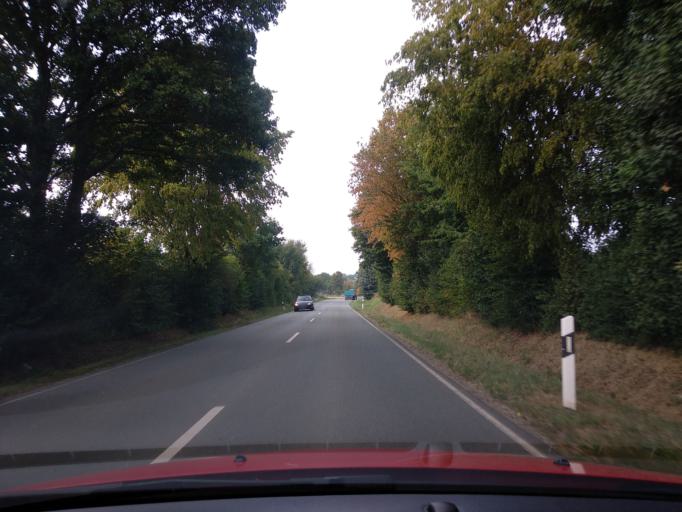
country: DE
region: Hesse
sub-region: Regierungsbezirk Kassel
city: Zierenberg
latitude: 51.4292
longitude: 9.3321
